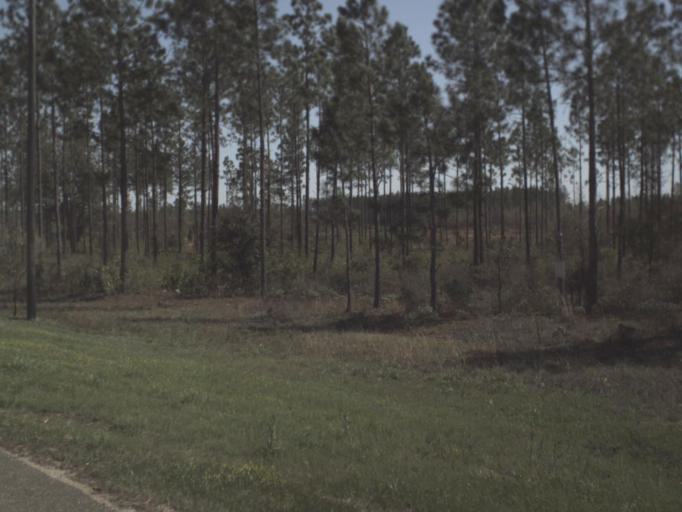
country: US
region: Florida
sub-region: Liberty County
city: Bristol
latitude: 30.4215
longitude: -84.9051
